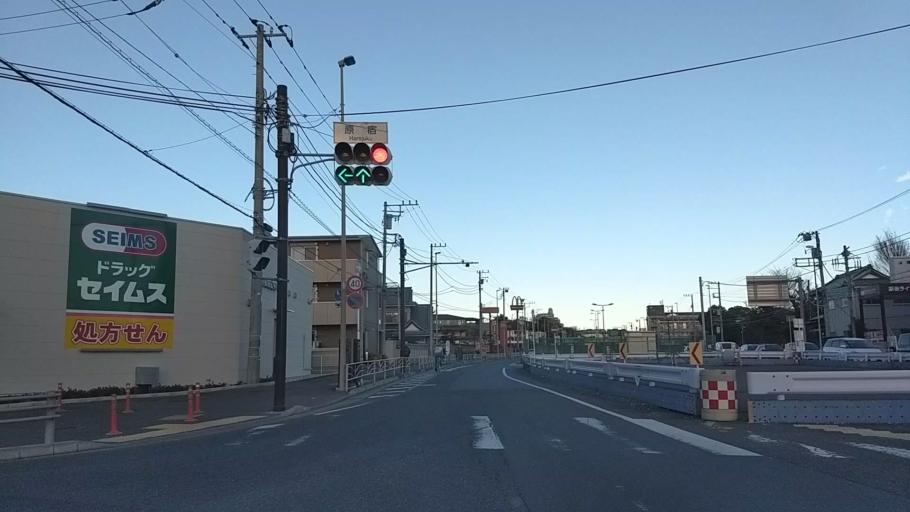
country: JP
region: Kanagawa
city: Fujisawa
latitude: 35.3772
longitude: 139.5052
